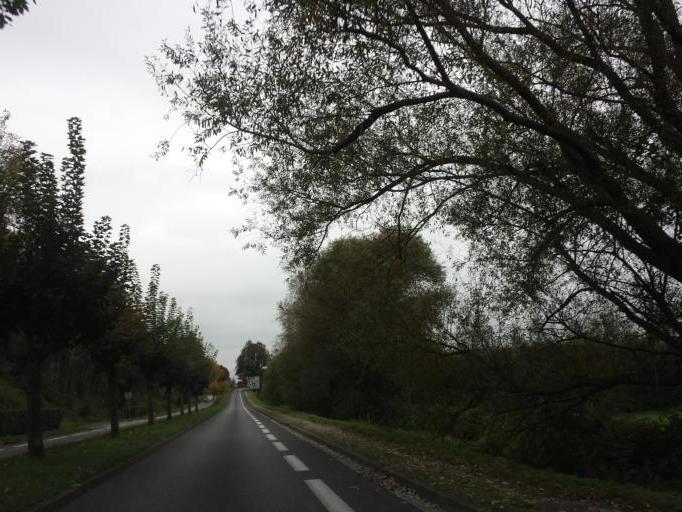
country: FR
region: Poitou-Charentes
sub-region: Departement de la Charente
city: La Couronne
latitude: 45.6262
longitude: 0.1149
